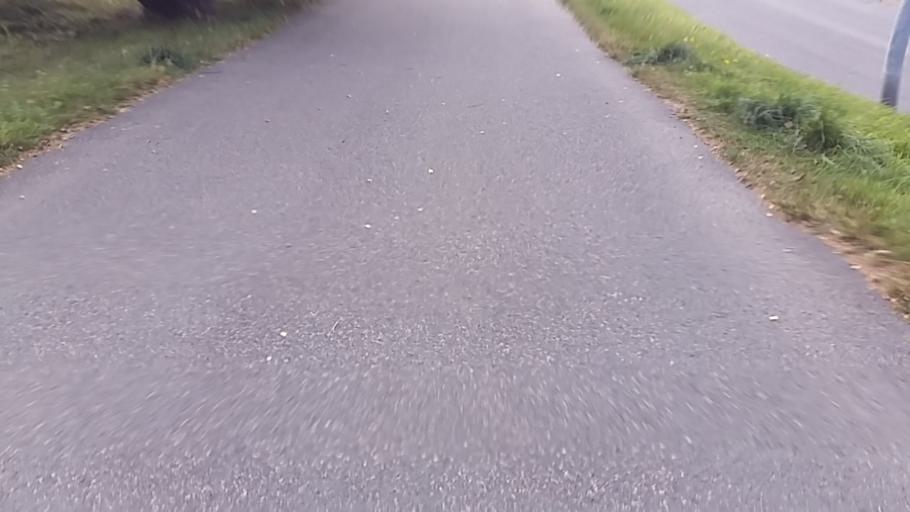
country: SE
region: Joenkoeping
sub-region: Jonkopings Kommun
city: Odensjo
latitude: 57.7380
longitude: 14.1542
